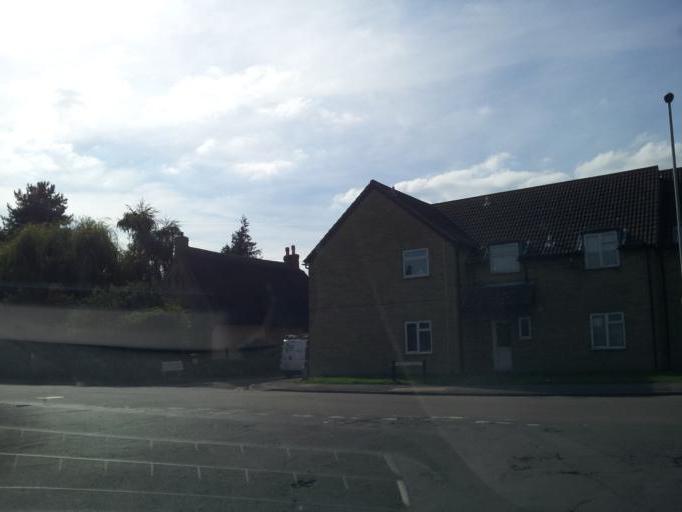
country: GB
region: England
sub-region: Cambridgeshire
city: Waterbeach
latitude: 52.2651
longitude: 0.1920
